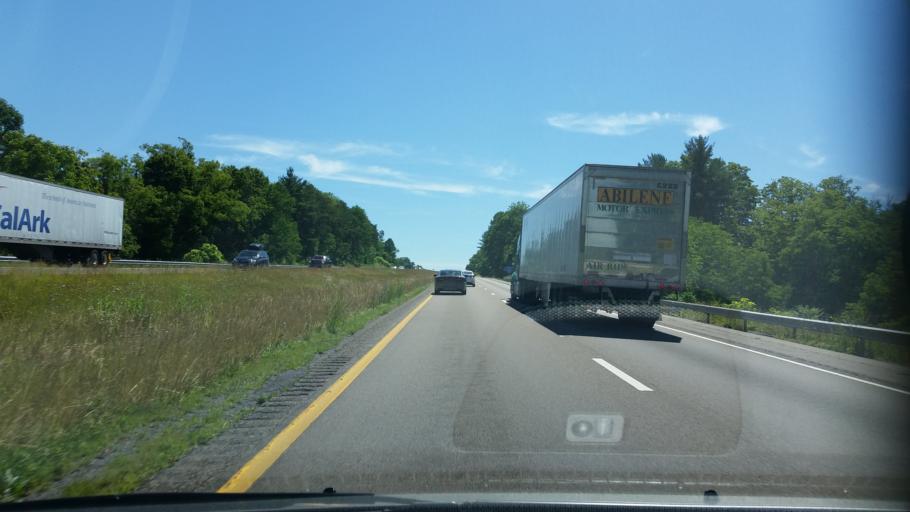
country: US
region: Virginia
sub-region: Smyth County
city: Adwolf
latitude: 36.8128
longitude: -81.6051
